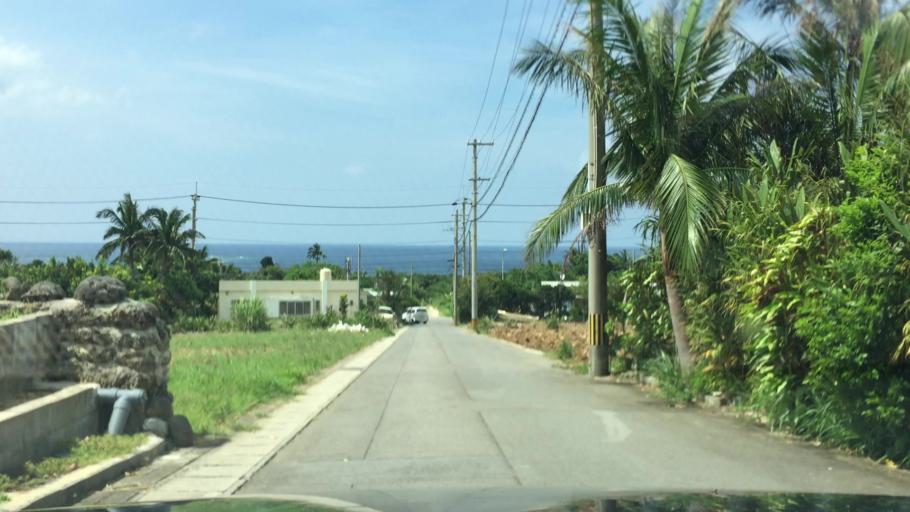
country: JP
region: Okinawa
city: Ishigaki
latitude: 24.4531
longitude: 124.1950
